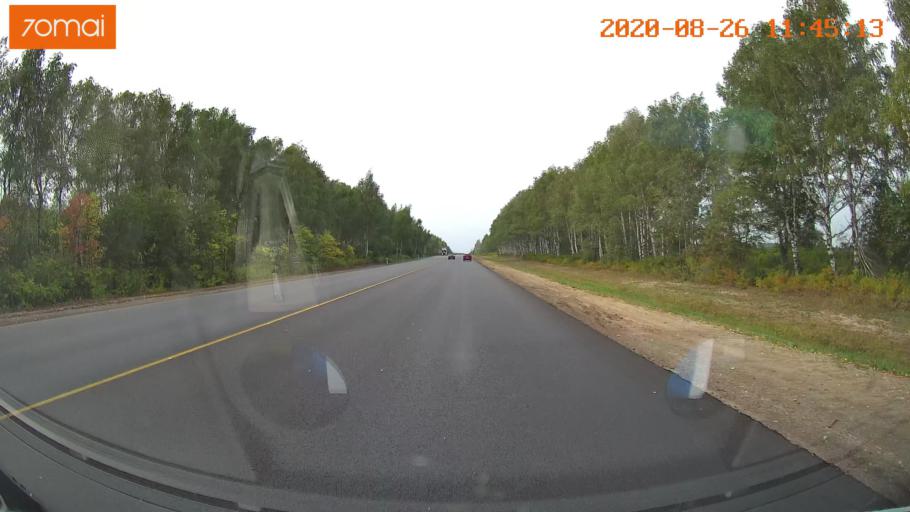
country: RU
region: Rjazan
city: Lesnoy
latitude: 54.2969
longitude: 40.6359
